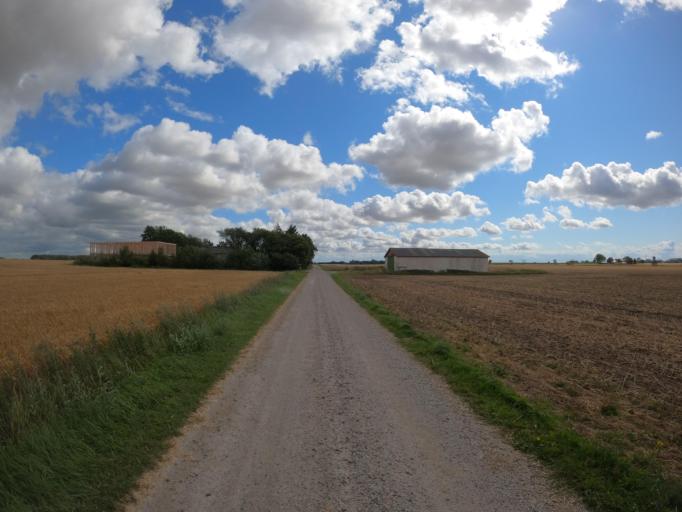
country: SE
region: Skane
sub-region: Lunds Kommun
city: Lund
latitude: 55.7316
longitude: 13.2614
